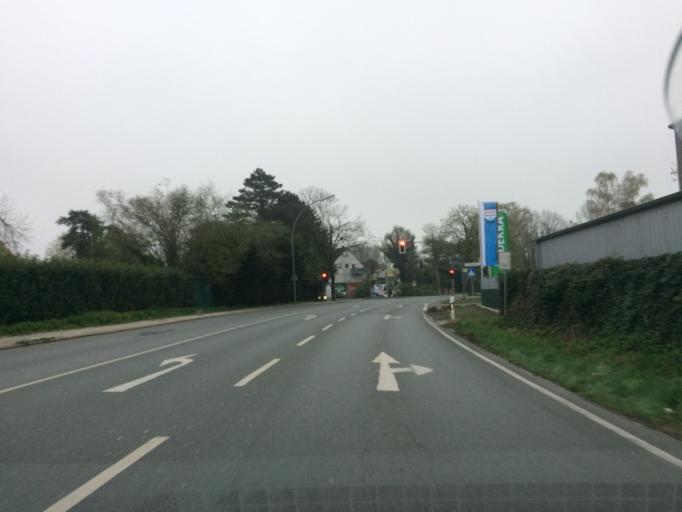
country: DE
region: North Rhine-Westphalia
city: Hattingen
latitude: 51.4455
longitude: 7.1635
